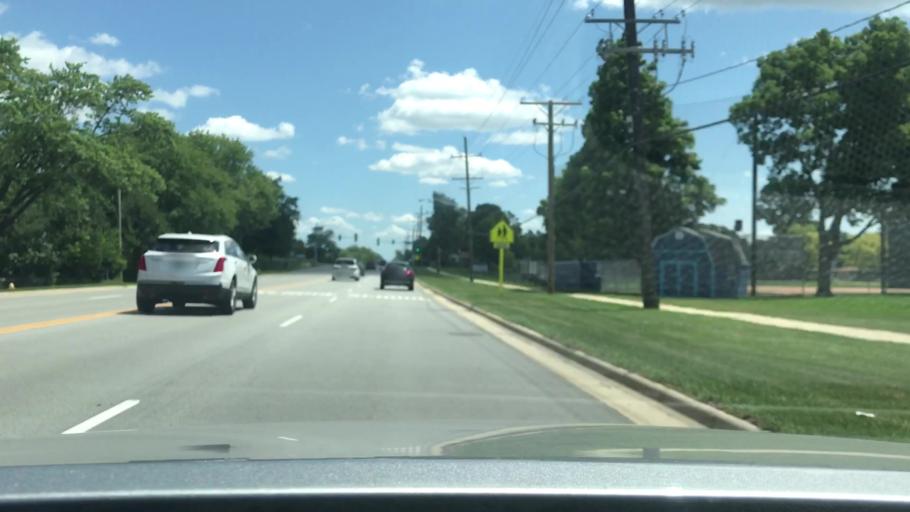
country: US
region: Illinois
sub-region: DuPage County
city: Downers Grove
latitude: 41.7727
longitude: -88.0208
